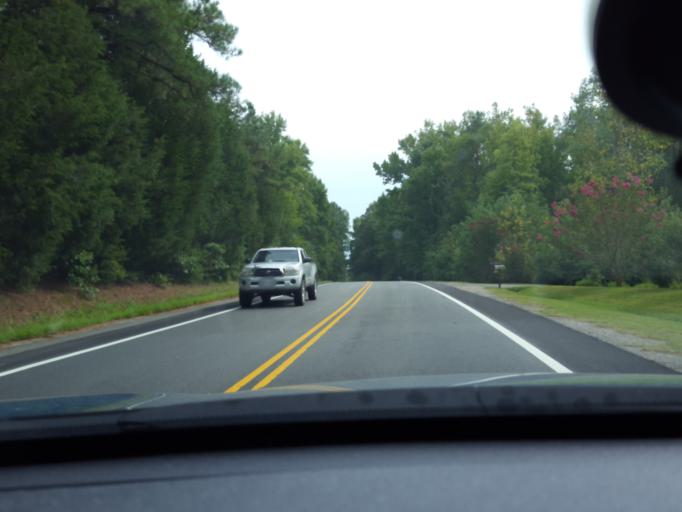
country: US
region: Virginia
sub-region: Hanover County
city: Hanover
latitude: 37.8112
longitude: -77.3741
